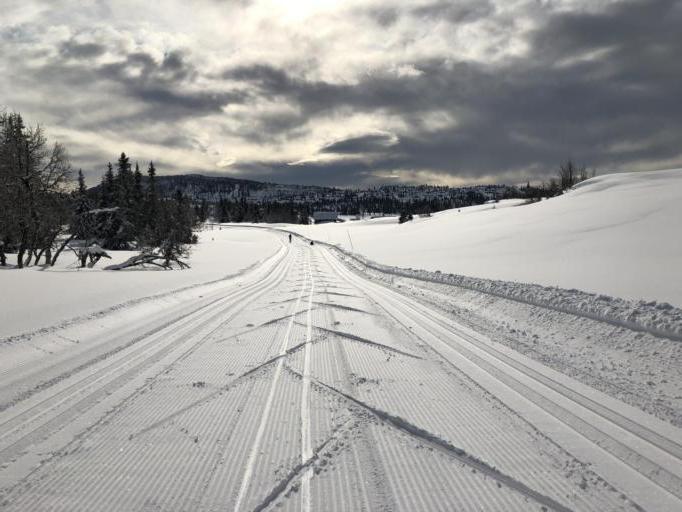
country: NO
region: Oppland
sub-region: Gausdal
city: Segalstad bru
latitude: 61.3179
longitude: 10.0592
